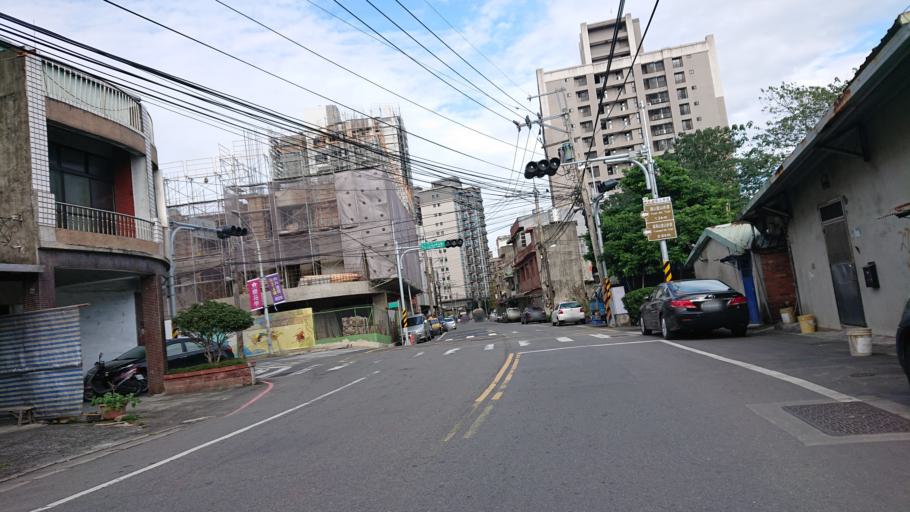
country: TW
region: Taiwan
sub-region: Taoyuan
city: Taoyuan
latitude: 24.9253
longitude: 121.3661
